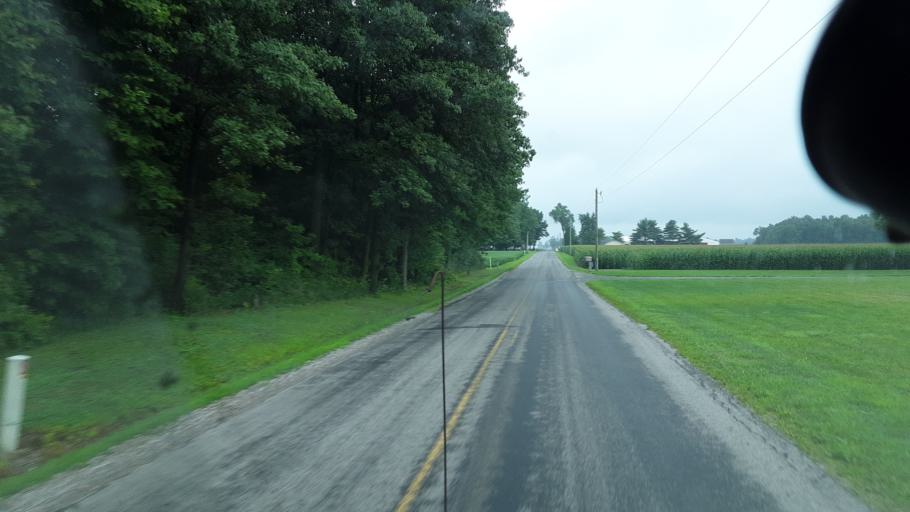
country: US
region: Indiana
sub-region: Wells County
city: Ossian
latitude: 40.8591
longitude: -85.1093
